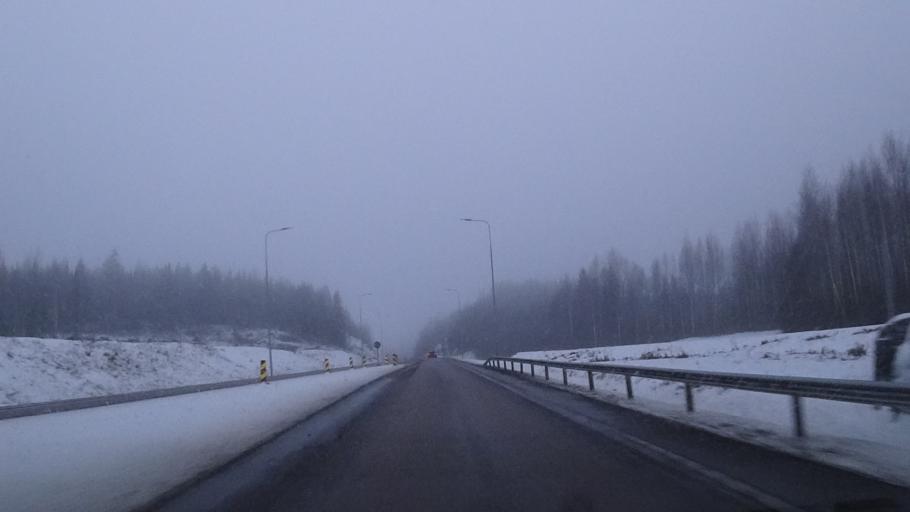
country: FI
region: Paijanne Tavastia
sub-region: Lahti
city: Hollola
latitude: 60.9809
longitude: 25.4803
